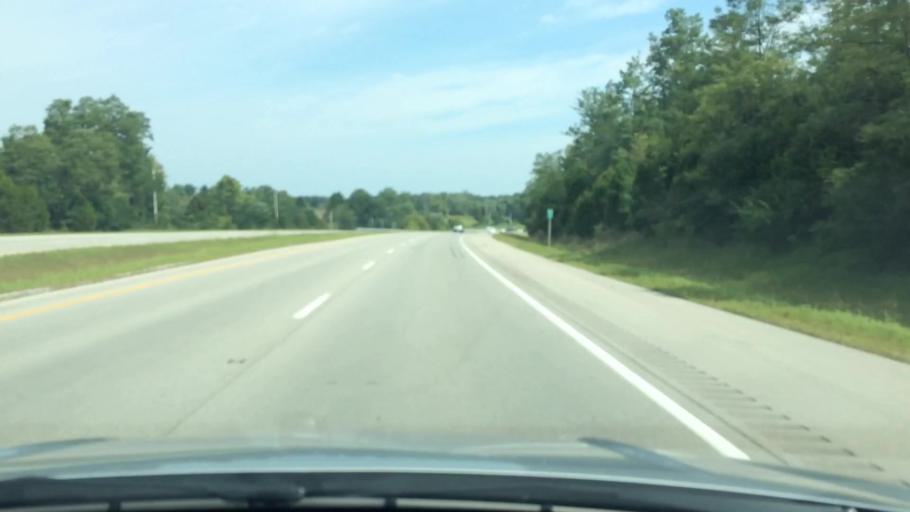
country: US
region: Kentucky
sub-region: Franklin County
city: Frankfort
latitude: 38.1279
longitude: -84.9146
